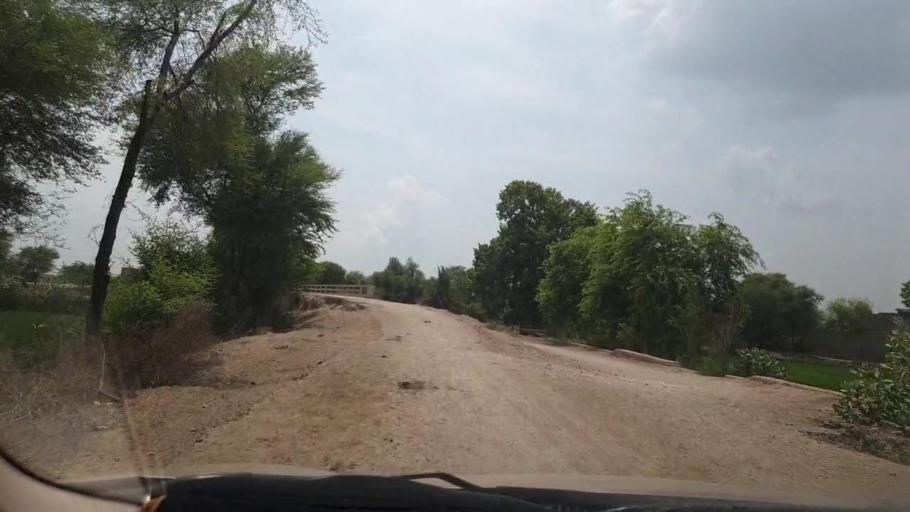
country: PK
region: Sindh
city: Larkana
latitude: 27.6047
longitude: 68.1248
